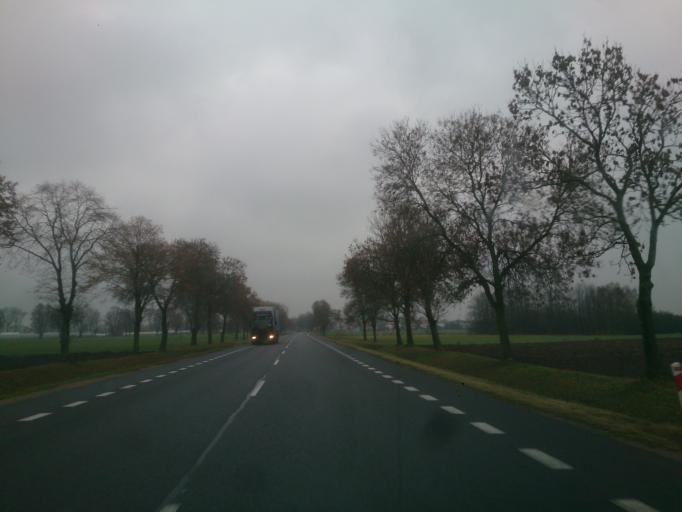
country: PL
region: Masovian Voivodeship
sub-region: Powiat plocki
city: Drobin
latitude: 52.7479
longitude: 19.9753
